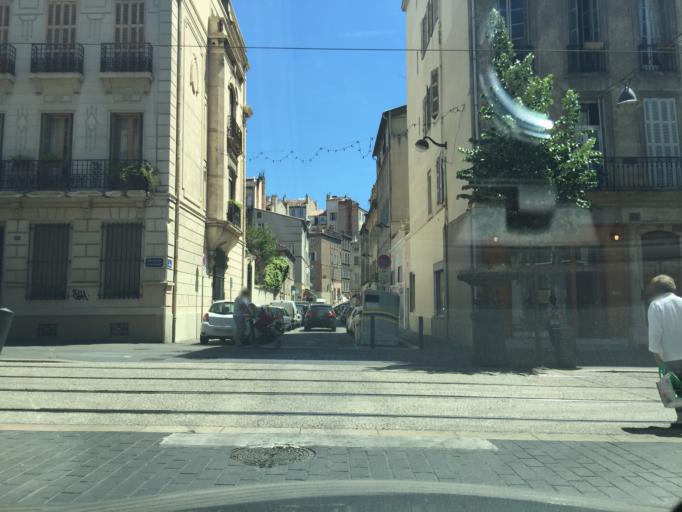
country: FR
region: Provence-Alpes-Cote d'Azur
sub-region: Departement des Bouches-du-Rhone
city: Marseille 01
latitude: 43.3024
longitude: 5.3903
